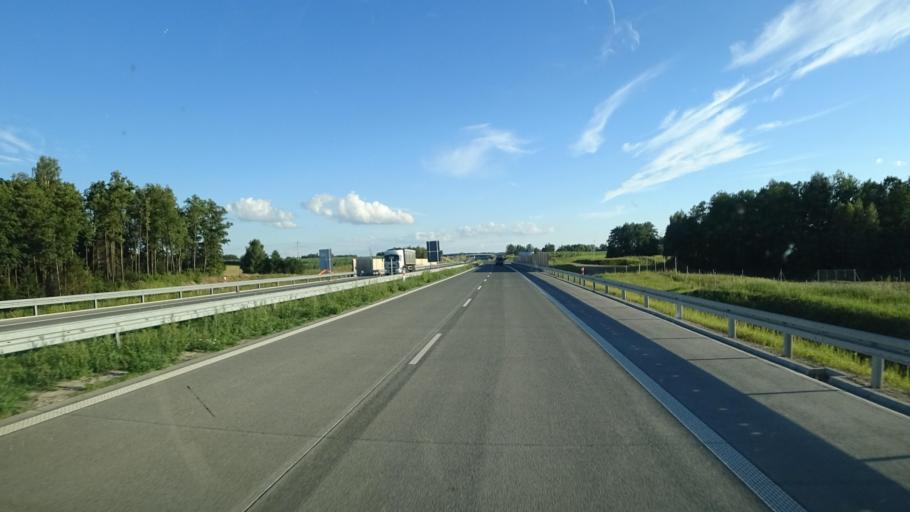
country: PL
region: Podlasie
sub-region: Powiat suwalski
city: Raczki
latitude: 53.9528
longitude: 22.7679
